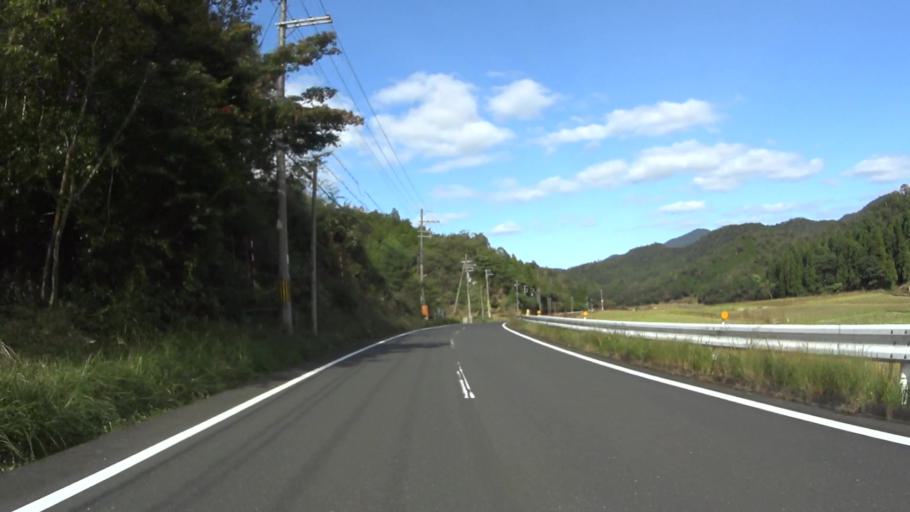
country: JP
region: Hyogo
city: Toyooka
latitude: 35.5528
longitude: 134.9771
